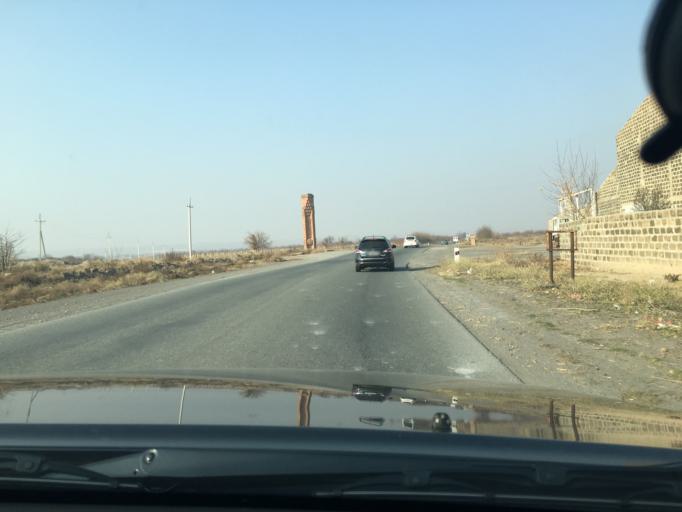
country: AM
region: Armavir
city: Myasnikyan
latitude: 40.1762
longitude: 43.9399
